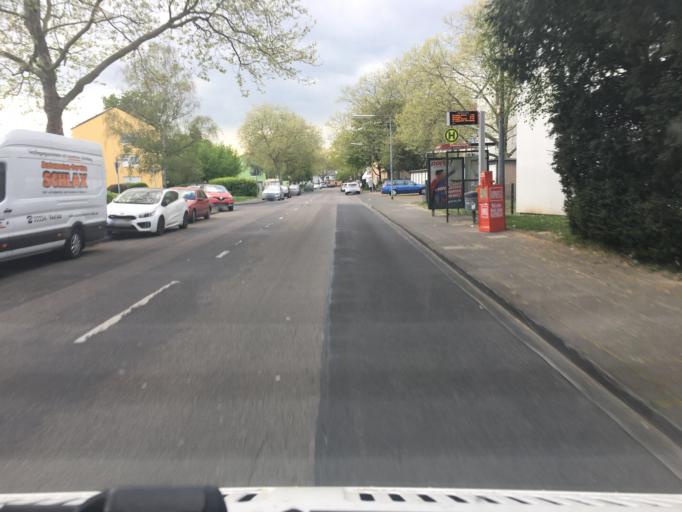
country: DE
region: North Rhine-Westphalia
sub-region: Regierungsbezirk Koln
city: Mengenich
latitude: 50.9633
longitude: 6.8760
